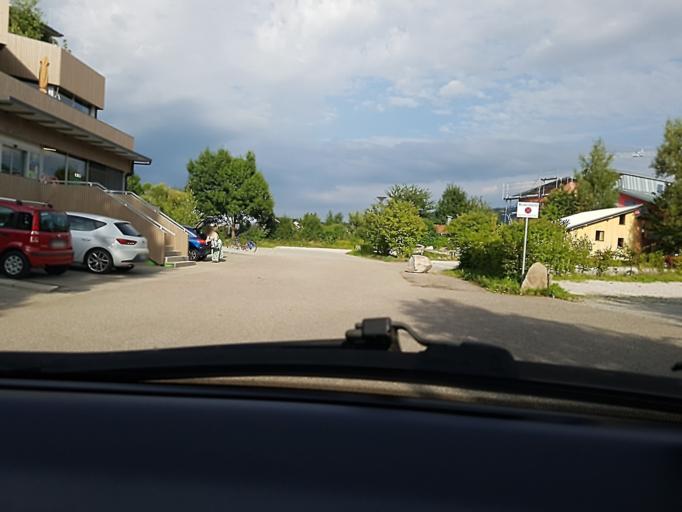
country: DE
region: Baden-Wuerttemberg
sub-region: Freiburg Region
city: Offenburg
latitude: 48.4851
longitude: 7.9597
